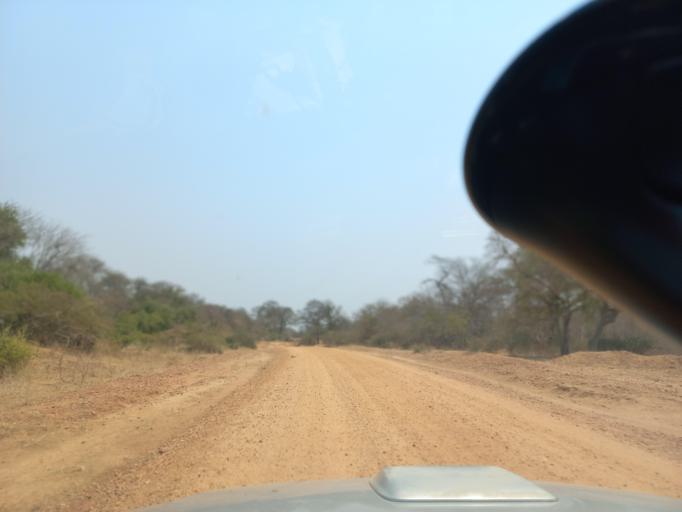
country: ZW
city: Chirundu
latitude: -15.9448
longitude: 28.8177
